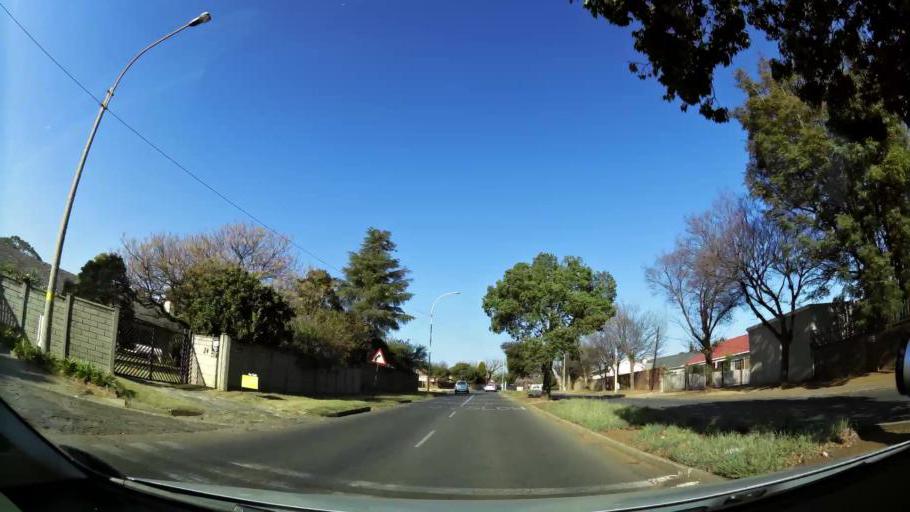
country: ZA
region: Gauteng
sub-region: City of Johannesburg Metropolitan Municipality
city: Modderfontein
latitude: -26.1514
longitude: 28.1626
